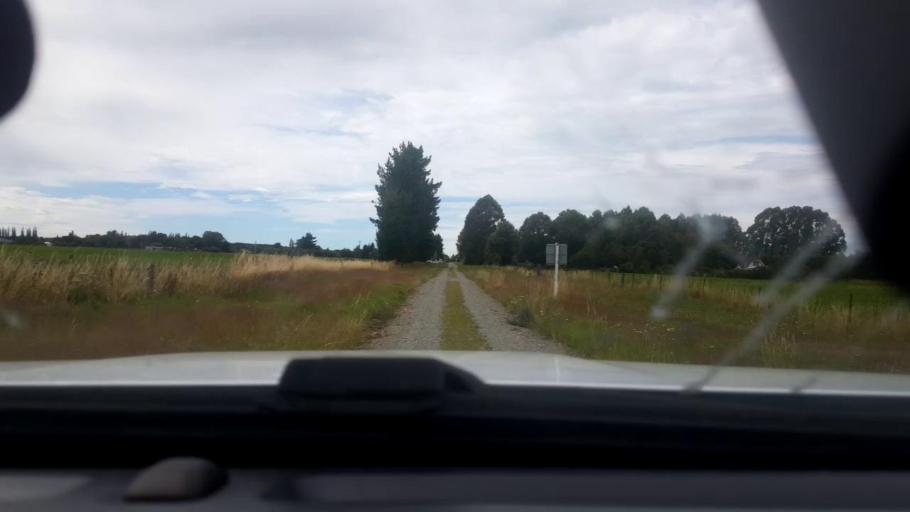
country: NZ
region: Canterbury
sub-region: Timaru District
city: Pleasant Point
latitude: -44.1337
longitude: 171.2857
